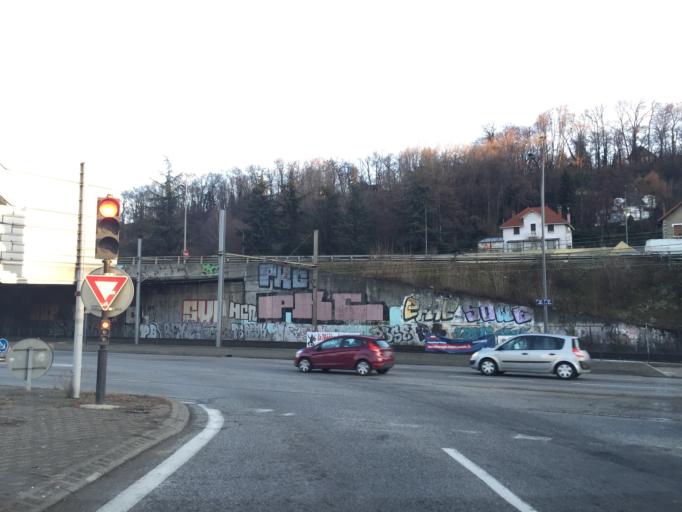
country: FR
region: Rhone-Alpes
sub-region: Departement de la Savoie
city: Cognin
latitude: 45.5835
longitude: 5.9096
